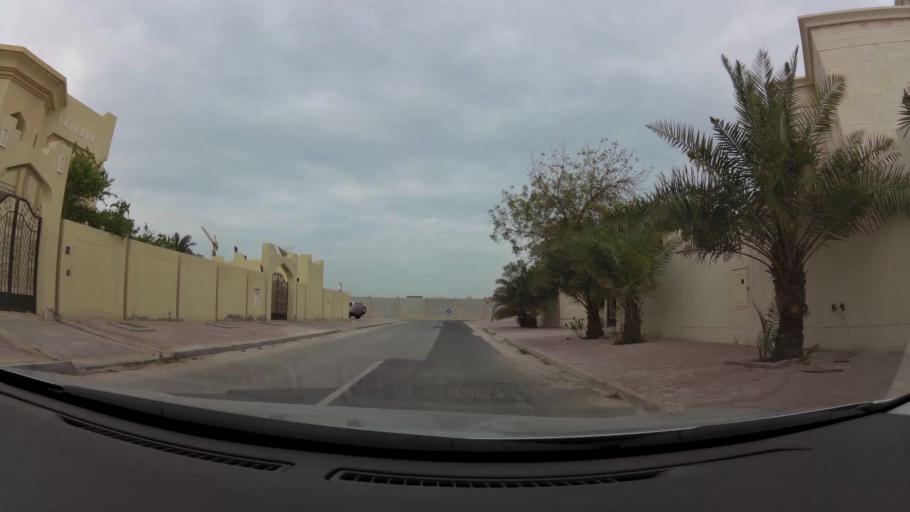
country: QA
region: Baladiyat ar Rayyan
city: Ar Rayyan
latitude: 25.3415
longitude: 51.4759
